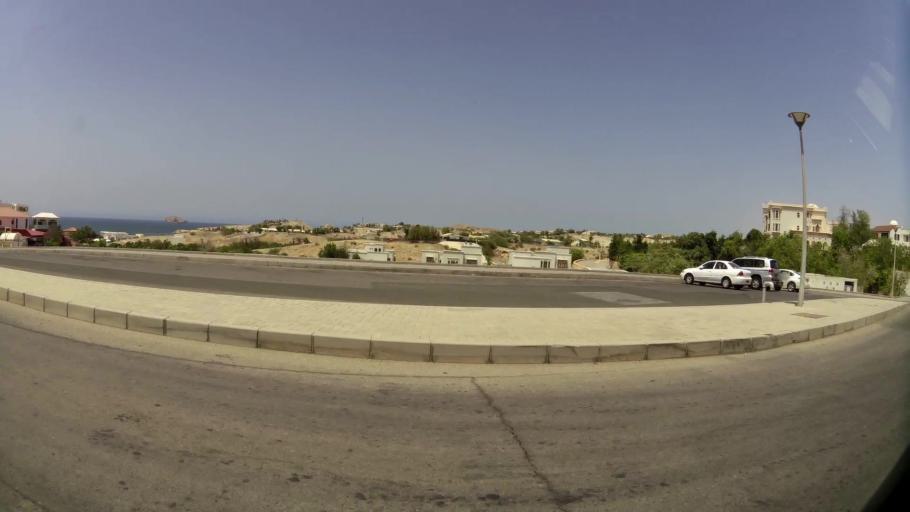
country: OM
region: Muhafazat Masqat
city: Muscat
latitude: 23.6302
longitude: 58.4879
